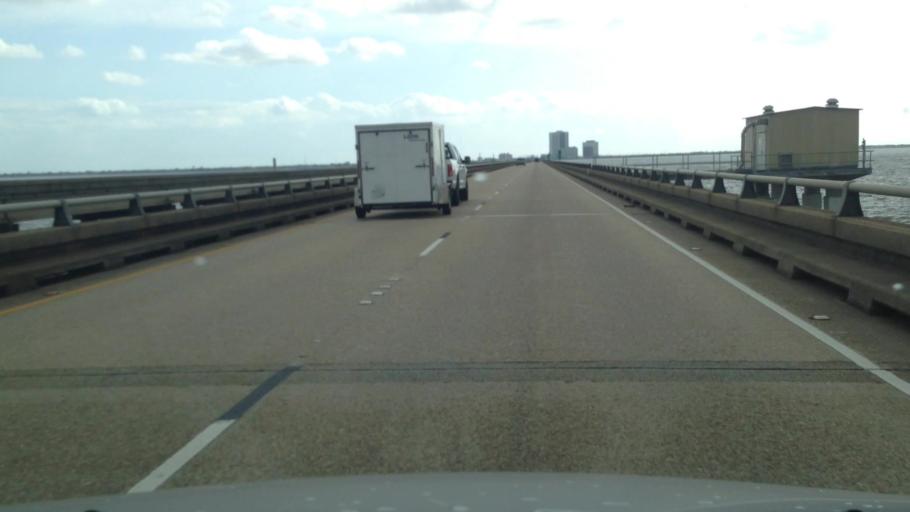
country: US
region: Louisiana
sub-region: Jefferson Parish
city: Metairie
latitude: 30.0546
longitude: -90.1483
